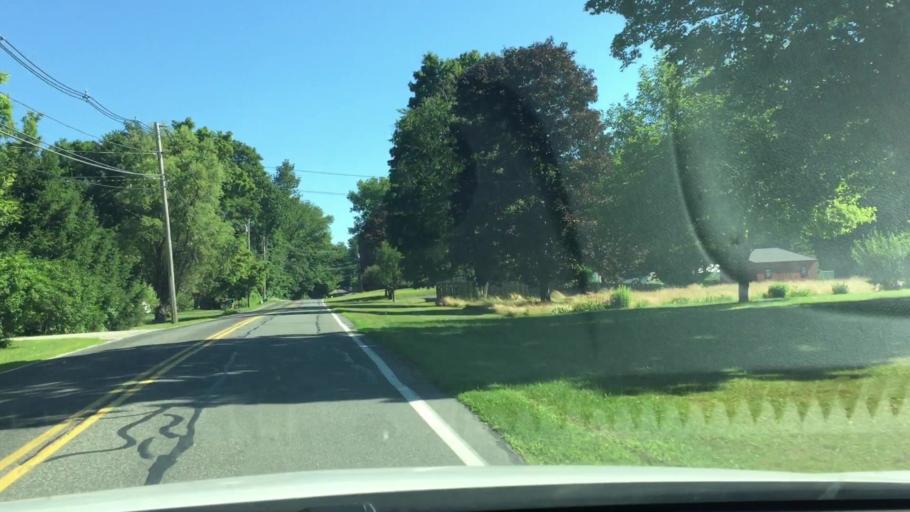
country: US
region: Massachusetts
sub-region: Berkshire County
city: West Stockbridge
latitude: 42.3396
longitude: -73.3670
